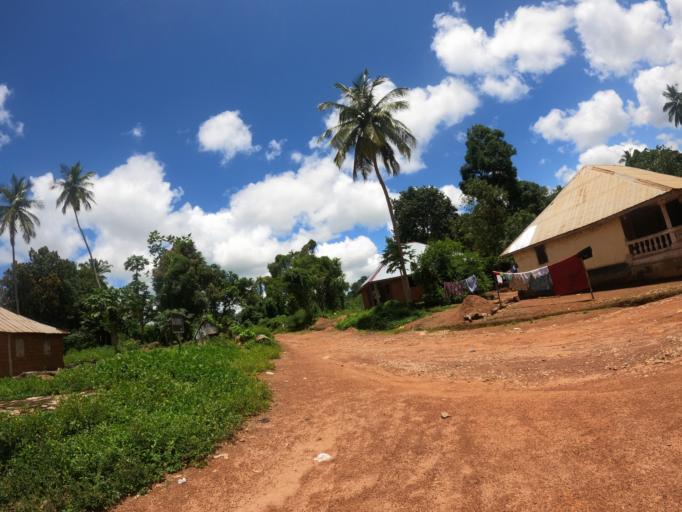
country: SL
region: Northern Province
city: Makeni
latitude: 8.8911
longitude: -12.0723
